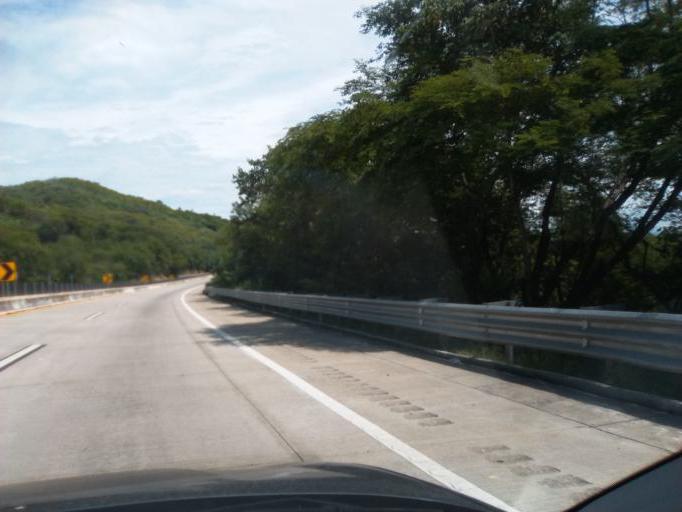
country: MX
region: Guerrero
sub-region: Acapulco de Juarez
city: Pueblo Madero (El Playon)
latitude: 17.0747
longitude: -99.6175
